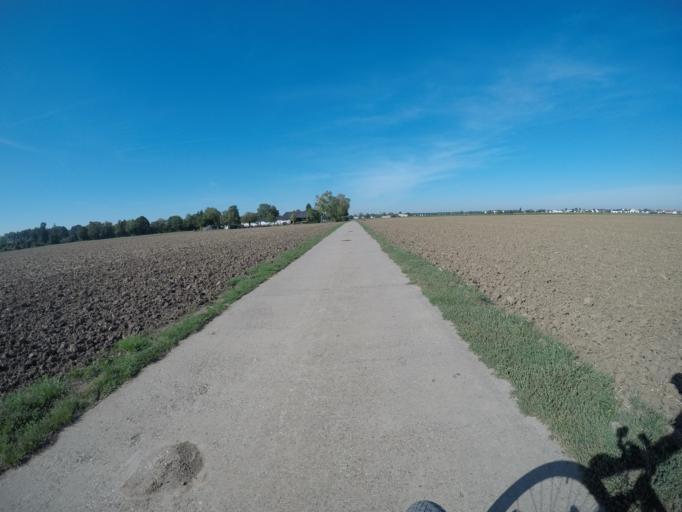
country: DE
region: Hesse
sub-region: Regierungsbezirk Darmstadt
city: Riedstadt
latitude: 49.8250
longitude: 8.5156
